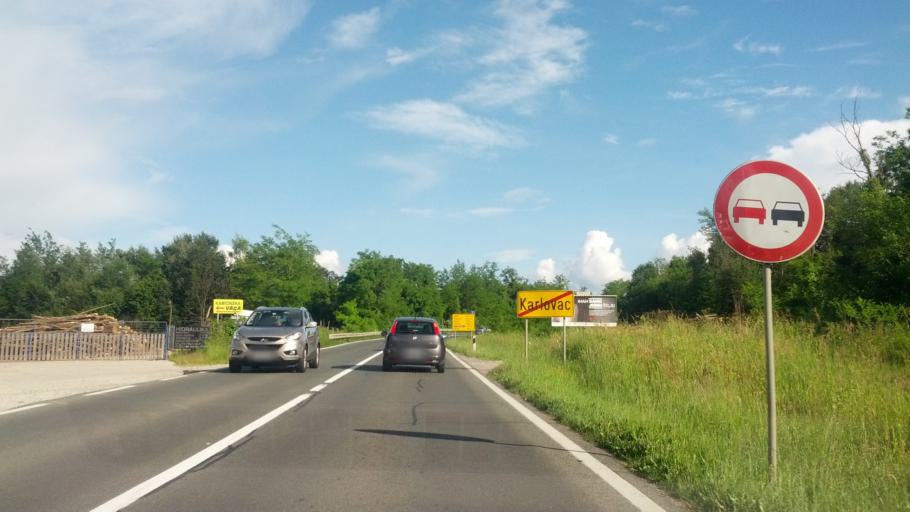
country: HR
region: Karlovacka
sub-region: Grad Karlovac
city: Karlovac
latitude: 45.4429
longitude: 15.5857
